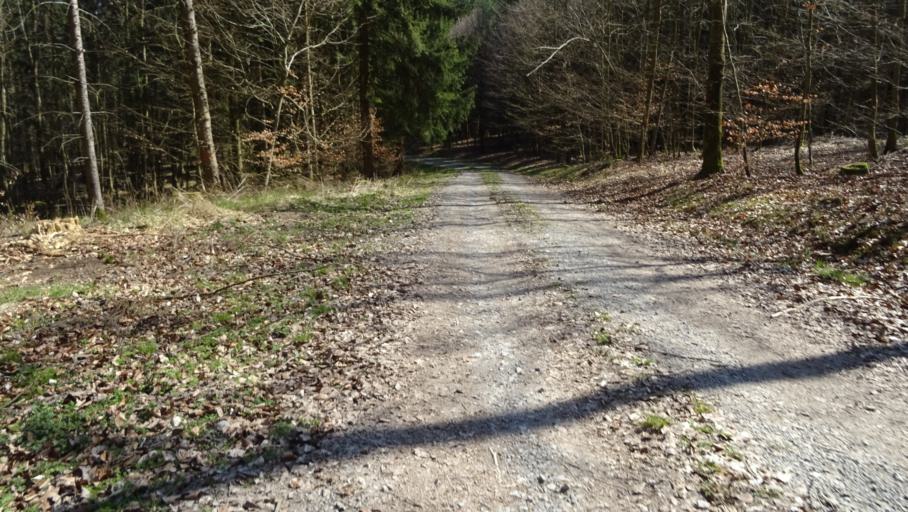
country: DE
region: Baden-Wuerttemberg
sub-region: Karlsruhe Region
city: Seckach
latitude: 49.4026
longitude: 9.3219
